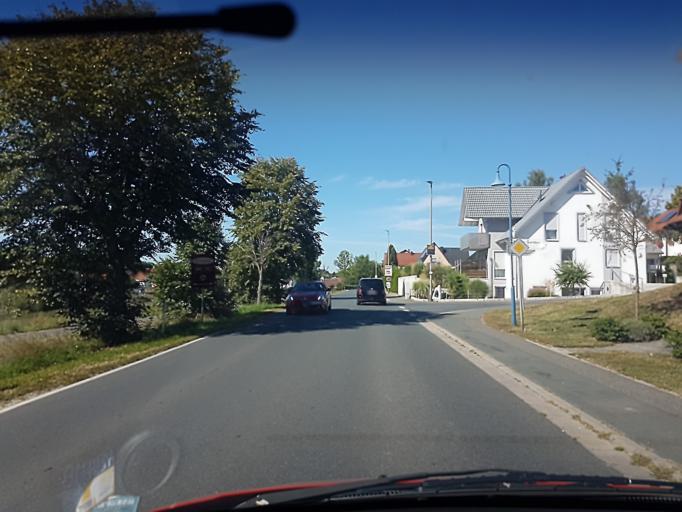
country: DE
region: Bavaria
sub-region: Upper Franconia
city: Heroldsbach
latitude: 49.6918
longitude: 11.0096
